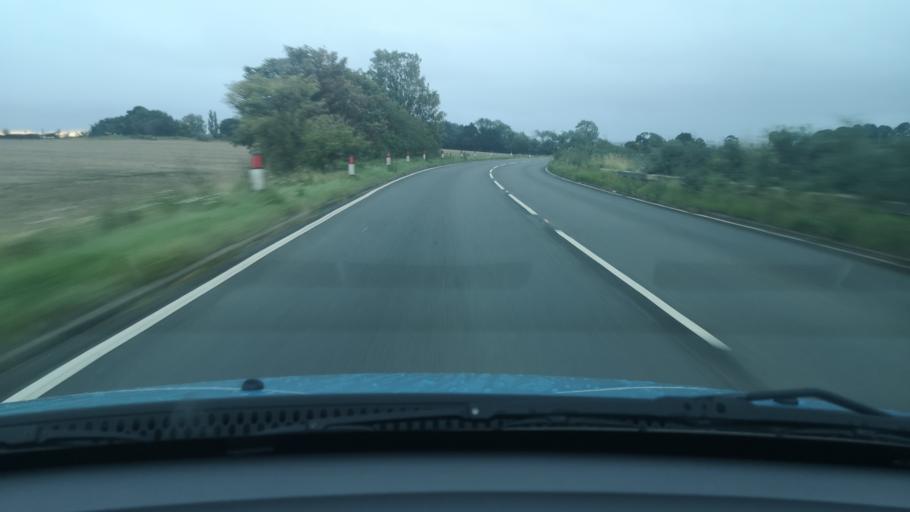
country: GB
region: England
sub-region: City and Borough of Wakefield
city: Badsworth
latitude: 53.6209
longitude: -1.3095
